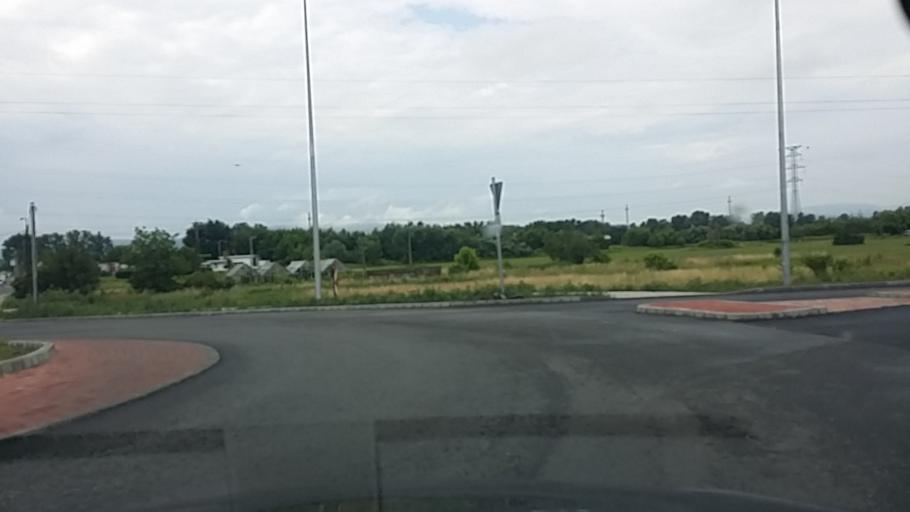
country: HU
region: Komarom-Esztergom
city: Esztergom
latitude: 47.7746
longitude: 18.7383
